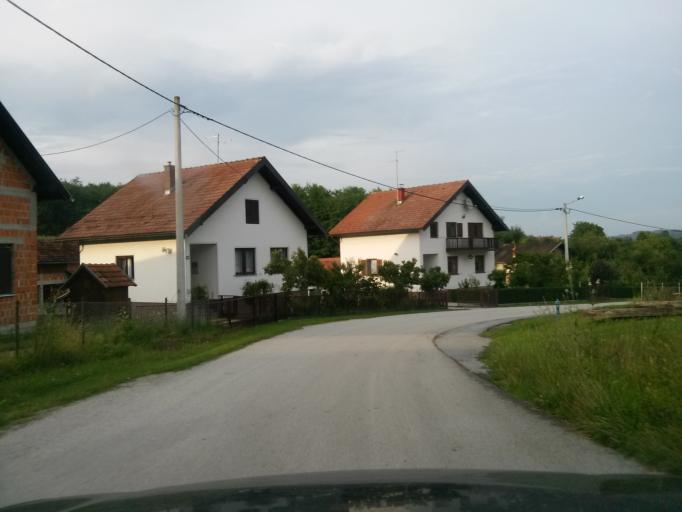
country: HR
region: Sisacko-Moslavacka
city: Gvozd
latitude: 45.2774
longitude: 15.9664
